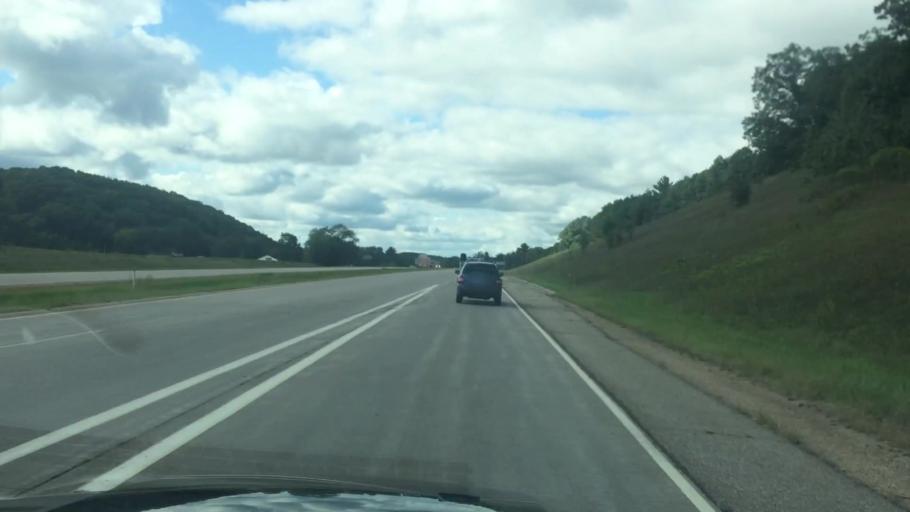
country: US
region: Wisconsin
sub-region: Waupaca County
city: Waupaca
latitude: 44.3407
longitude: -89.0729
